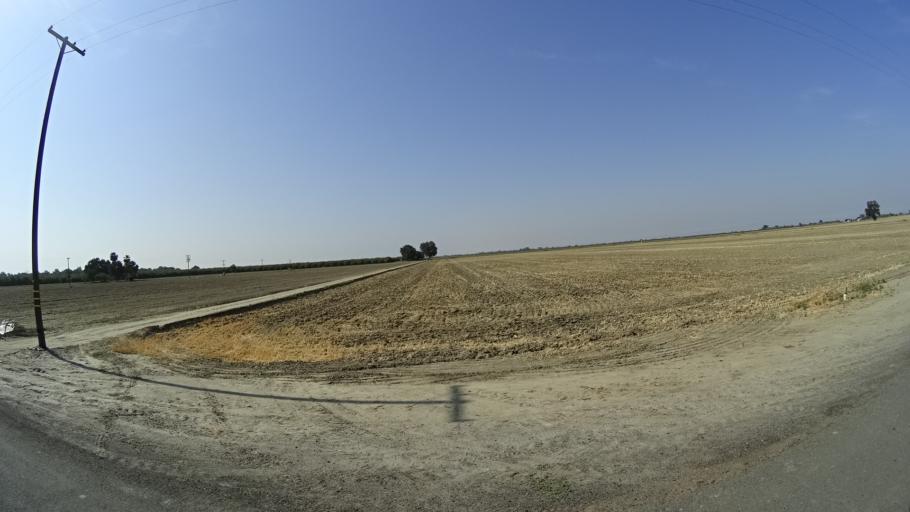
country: US
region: California
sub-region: Kings County
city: Lemoore Station
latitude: 36.3366
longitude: -119.8625
